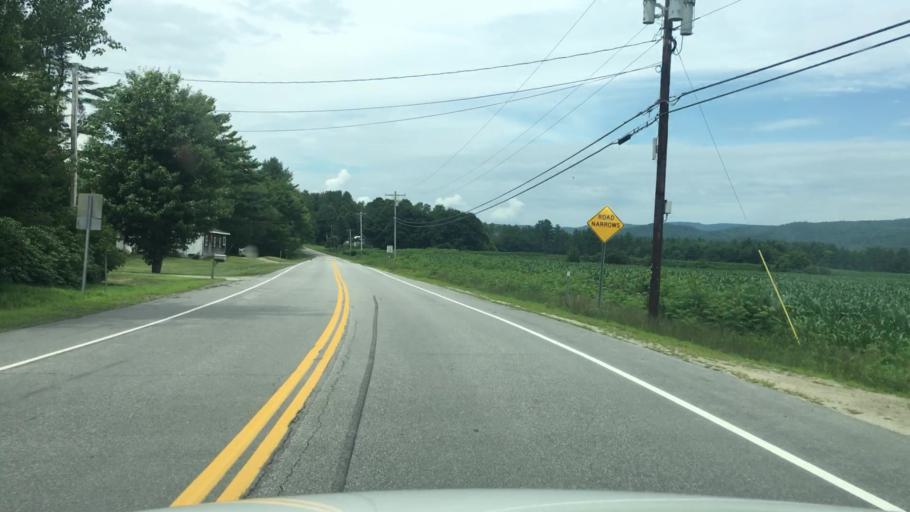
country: US
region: New Hampshire
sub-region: Grafton County
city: Plymouth
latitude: 43.7776
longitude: -71.7432
